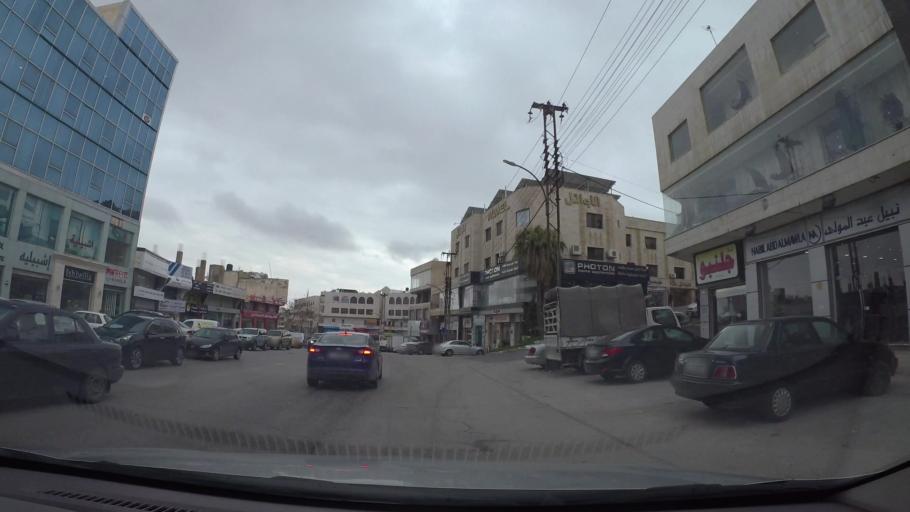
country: JO
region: Amman
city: Wadi as Sir
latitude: 31.9781
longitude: 35.8492
